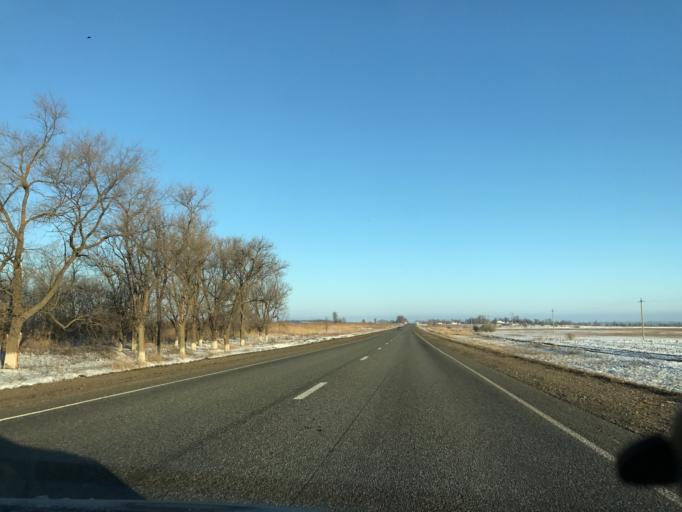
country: RU
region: Stavropol'skiy
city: Bezopasnoye
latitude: 45.5801
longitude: 41.9473
